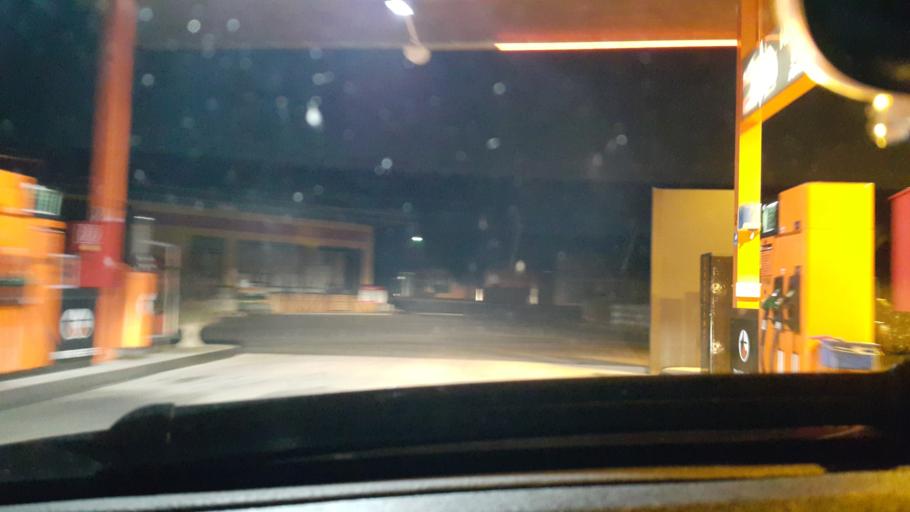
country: AT
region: Styria
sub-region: Politischer Bezirk Leibnitz
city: Leutschach
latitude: 46.6612
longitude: 15.4700
